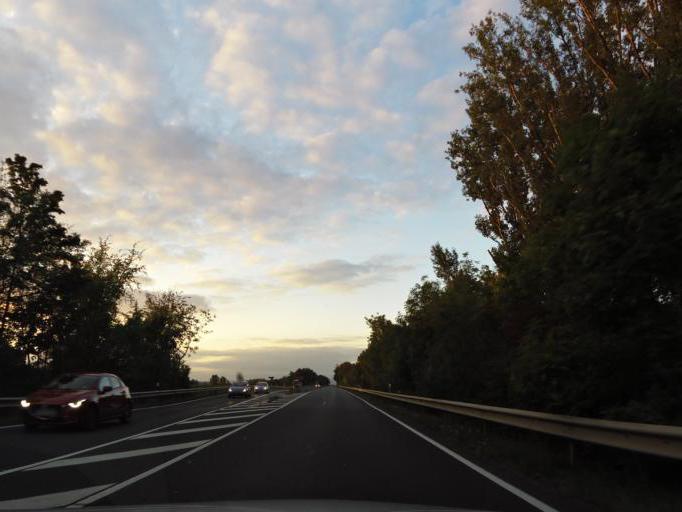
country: DE
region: Rheinland-Pfalz
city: Nackenheim
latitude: 49.9234
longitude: 8.3451
